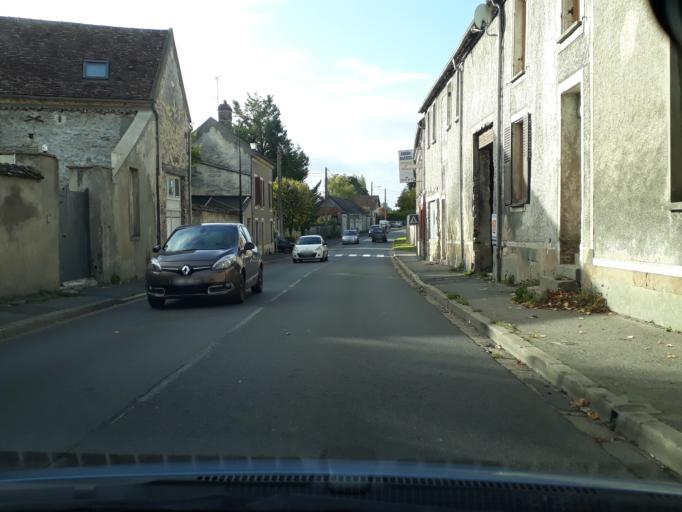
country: FR
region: Ile-de-France
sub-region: Departement de Seine-et-Marne
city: Acheres-la-Foret
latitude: 48.3424
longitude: 2.6013
